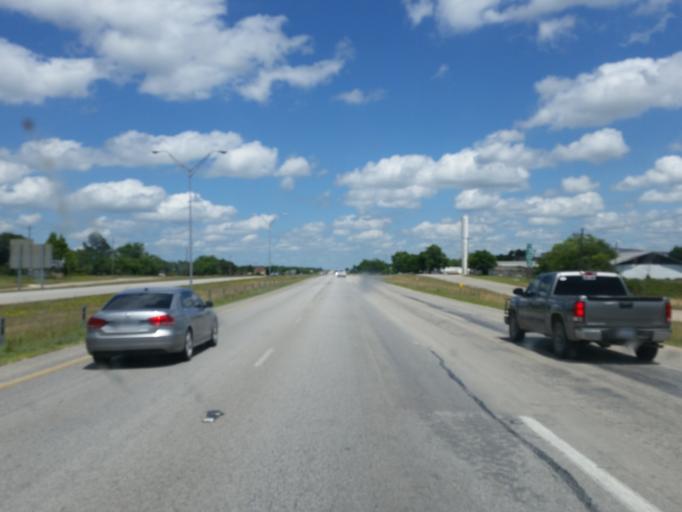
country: US
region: Texas
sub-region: Callahan County
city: Clyde
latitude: 32.4112
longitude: -99.4851
